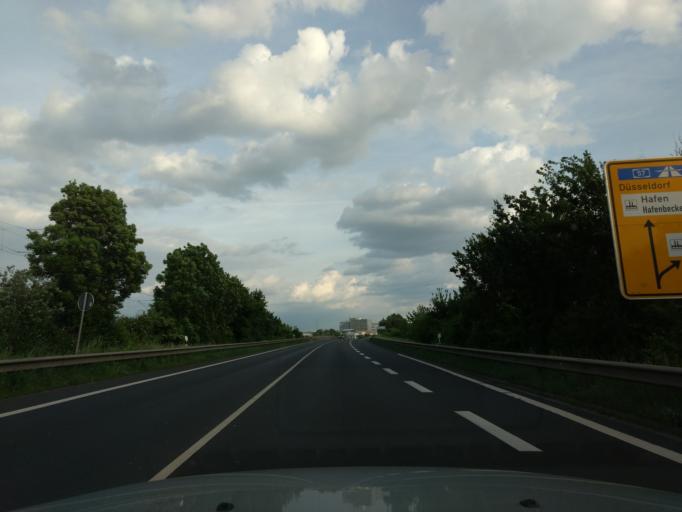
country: DE
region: North Rhine-Westphalia
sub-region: Regierungsbezirk Dusseldorf
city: Neuss
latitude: 51.2083
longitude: 6.7118
